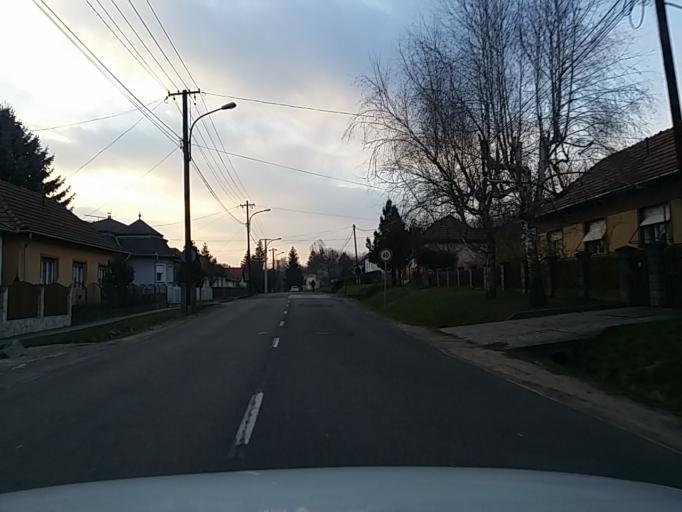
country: HU
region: Nograd
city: Matraterenye
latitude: 48.0044
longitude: 19.9088
